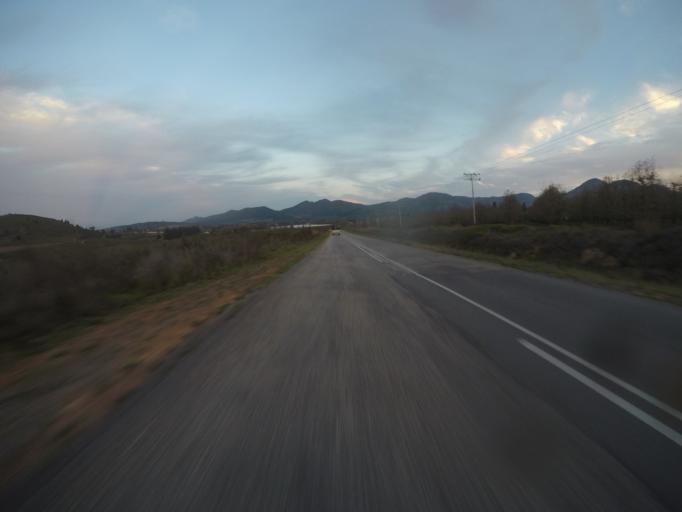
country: ZA
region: Western Cape
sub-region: Eden District Municipality
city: Plettenberg Bay
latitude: -33.7474
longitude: 23.4804
